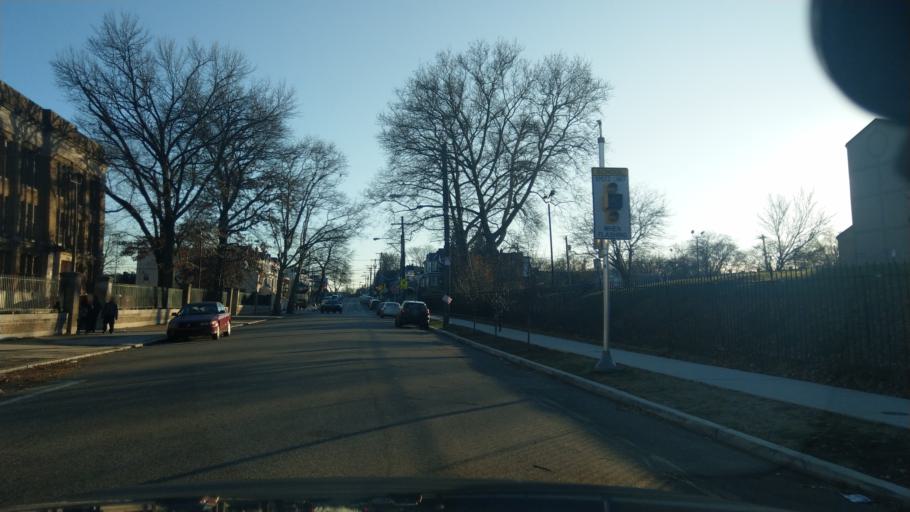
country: US
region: Pennsylvania
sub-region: Montgomery County
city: Wyncote
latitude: 40.0523
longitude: -75.1484
